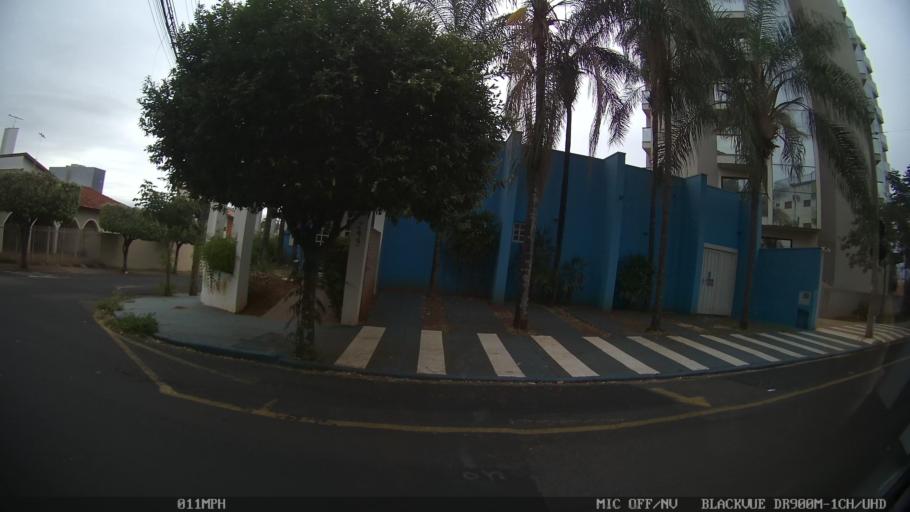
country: BR
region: Sao Paulo
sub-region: Sao Jose Do Rio Preto
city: Sao Jose do Rio Preto
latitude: -20.8307
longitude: -49.3884
